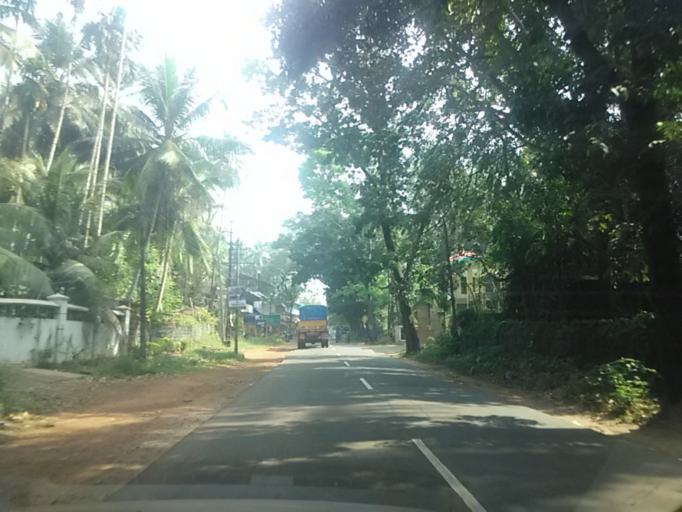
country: IN
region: Kerala
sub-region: Kozhikode
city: Kunnamangalam
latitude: 11.3148
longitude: 75.9252
